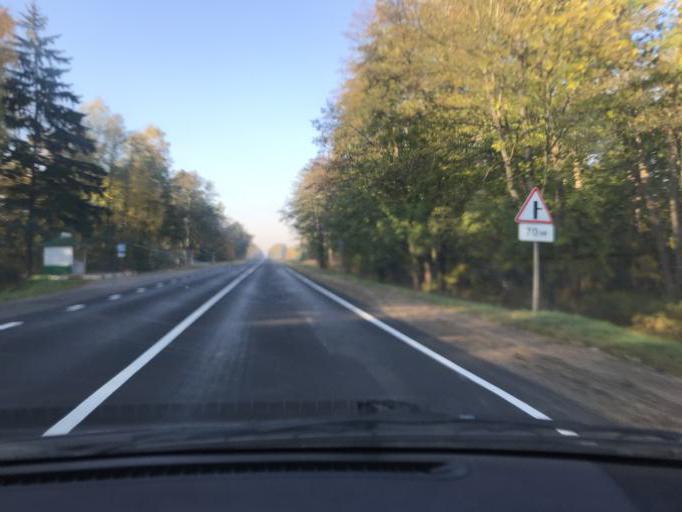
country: BY
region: Brest
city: Baranovichi
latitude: 52.8811
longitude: 25.7715
